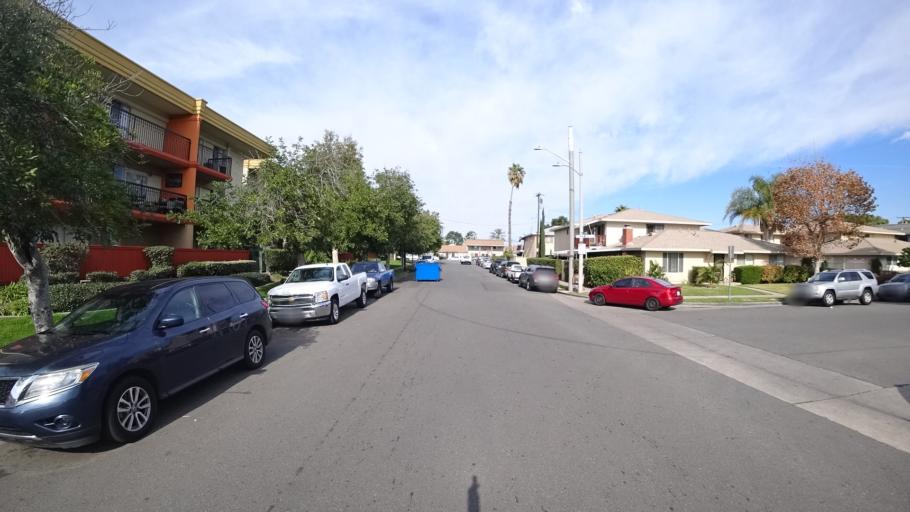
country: US
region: California
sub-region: Orange County
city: Garden Grove
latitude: 33.7880
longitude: -117.9034
